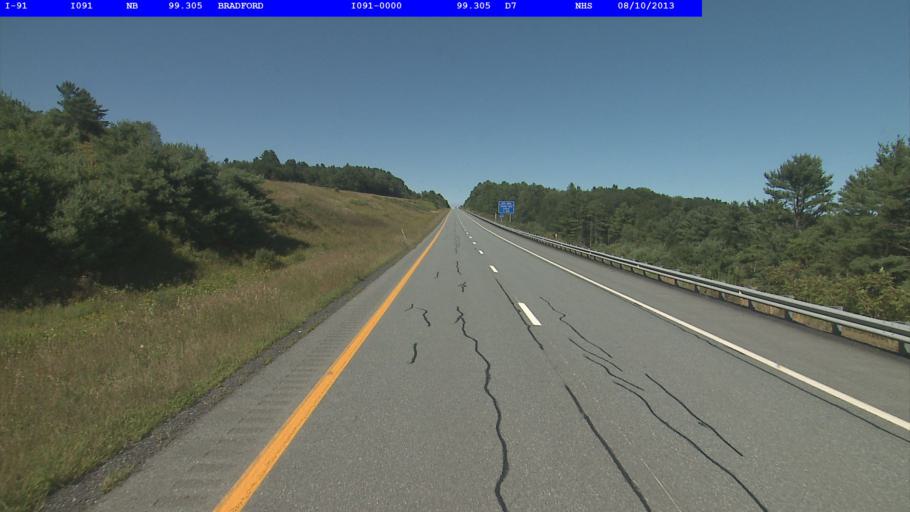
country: US
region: New Hampshire
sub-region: Grafton County
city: Haverhill
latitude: 44.0058
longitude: -72.1265
